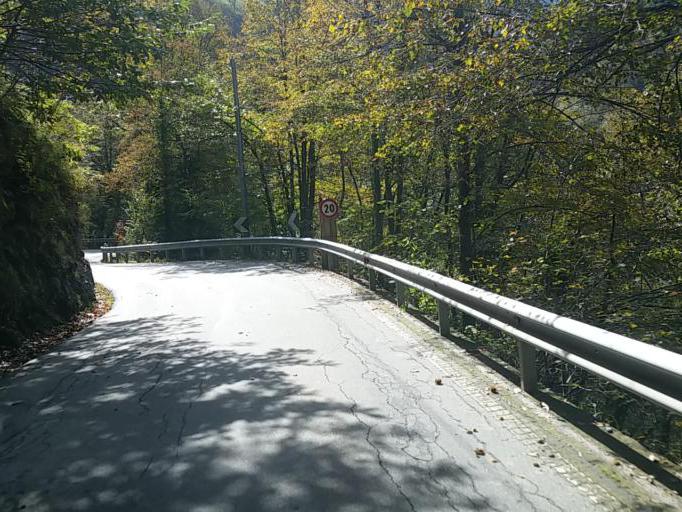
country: IT
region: Piedmont
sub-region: Provincia Verbano-Cusio-Ossola
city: Falmenta
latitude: 46.0736
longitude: 8.6018
